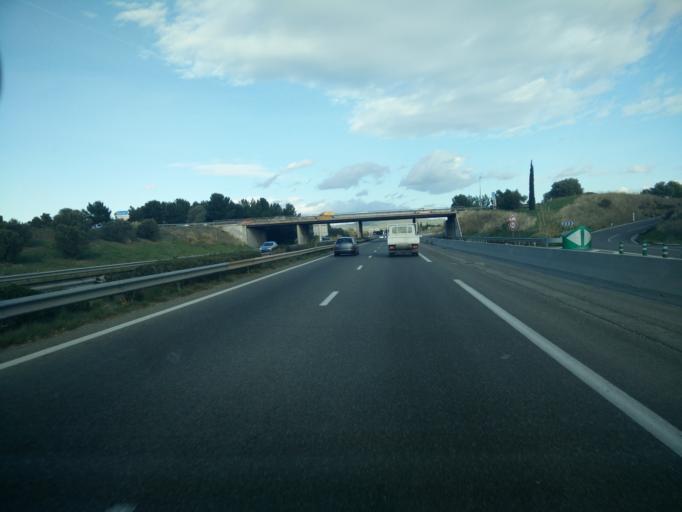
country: FR
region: Provence-Alpes-Cote d'Azur
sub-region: Departement du Var
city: La Farlede
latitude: 43.1572
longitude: 6.0447
